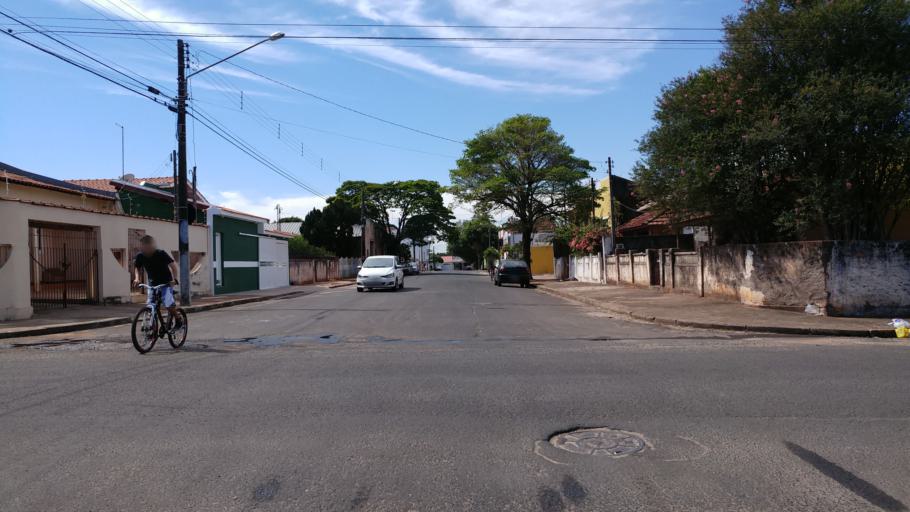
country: BR
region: Sao Paulo
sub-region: Paraguacu Paulista
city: Paraguacu Paulista
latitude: -22.4108
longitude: -50.5743
